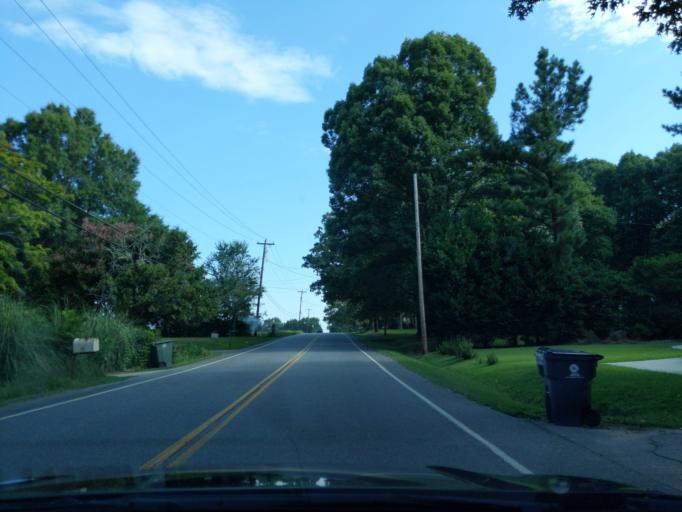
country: US
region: South Carolina
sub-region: Greenville County
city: Mauldin
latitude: 34.8092
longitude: -82.3109
